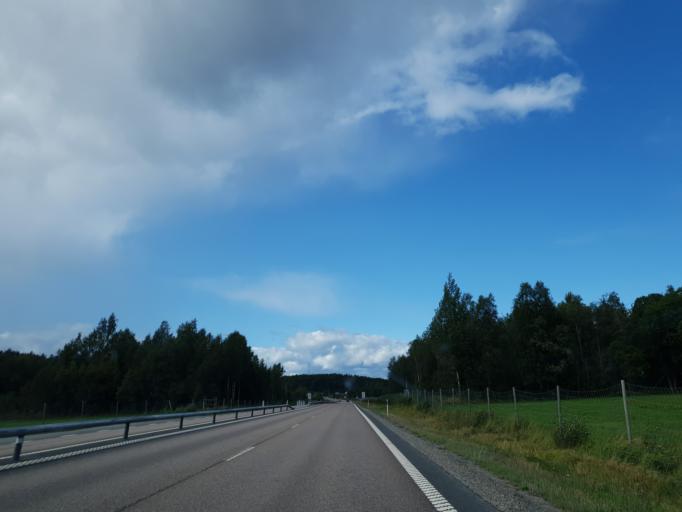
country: SE
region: Vaesternorrland
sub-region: OErnskoeldsviks Kommun
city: Ornskoldsvik
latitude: 63.3053
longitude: 18.8521
